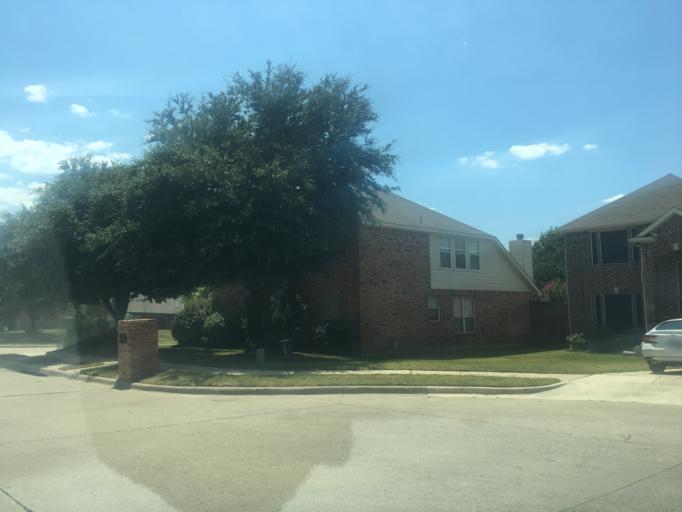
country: US
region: Texas
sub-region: Denton County
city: Lewisville
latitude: 33.0149
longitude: -97.0007
